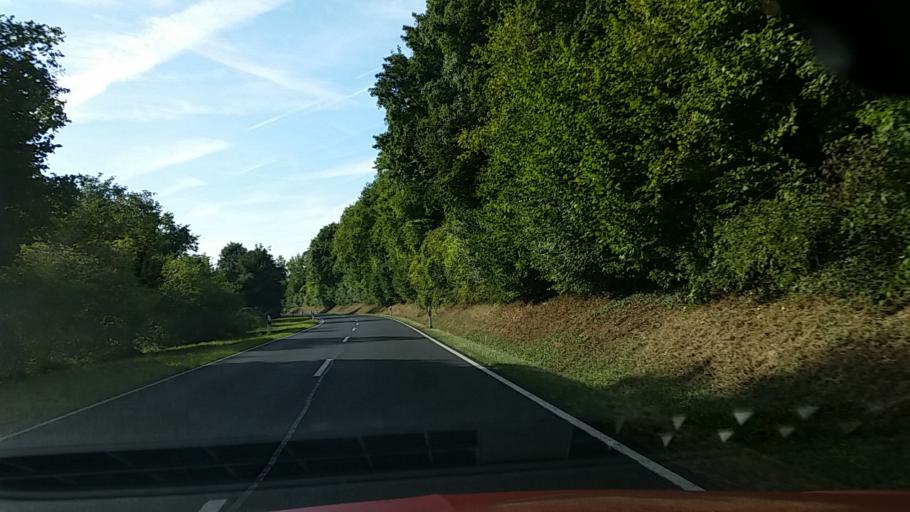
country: DE
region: Bavaria
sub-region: Regierungsbezirk Unterfranken
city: Himmelstadt
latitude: 49.9104
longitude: 9.7995
